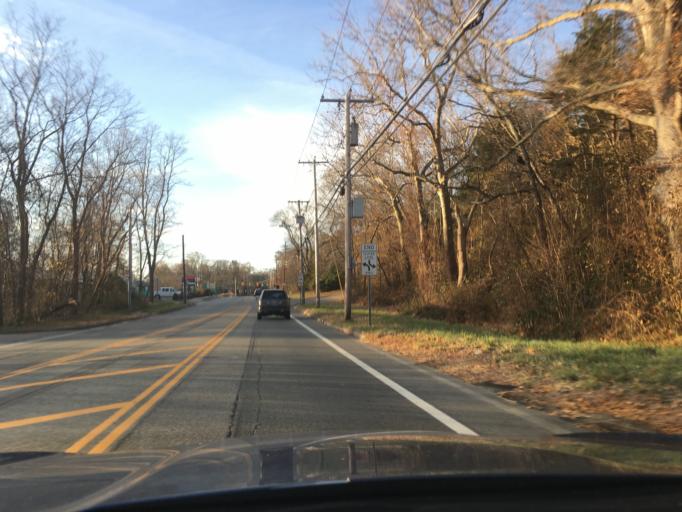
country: US
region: Rhode Island
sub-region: Washington County
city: North Kingstown
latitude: 41.5764
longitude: -71.4609
